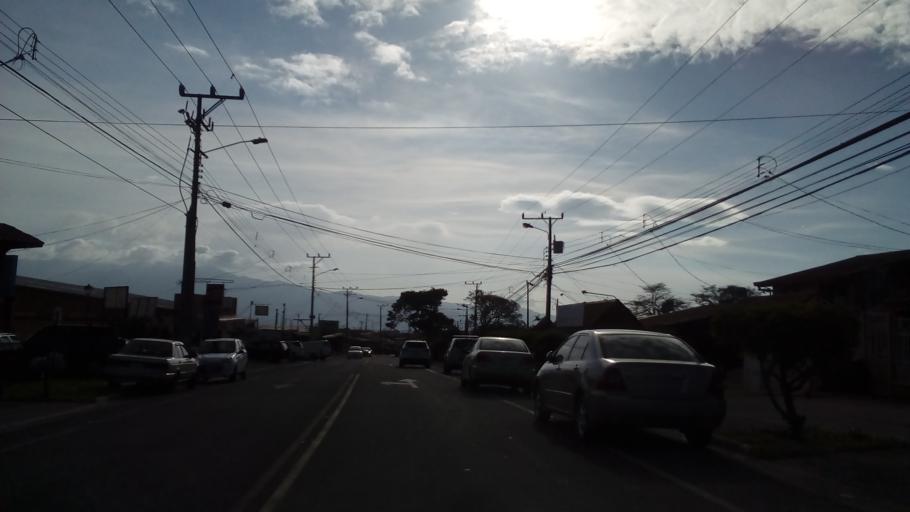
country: CR
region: Heredia
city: Angeles
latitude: 9.9907
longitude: -84.0574
